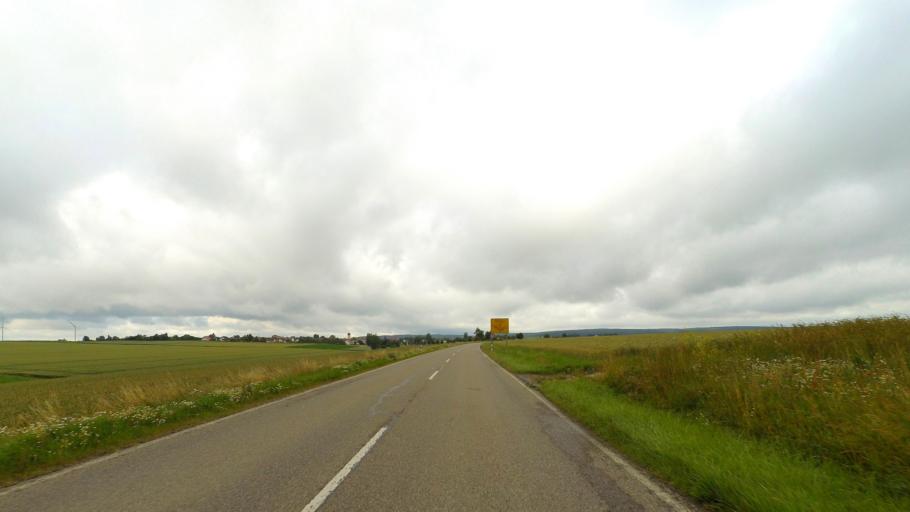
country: DE
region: Baden-Wuerttemberg
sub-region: Tuebingen Region
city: Neenstetten
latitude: 48.5475
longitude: 10.0330
